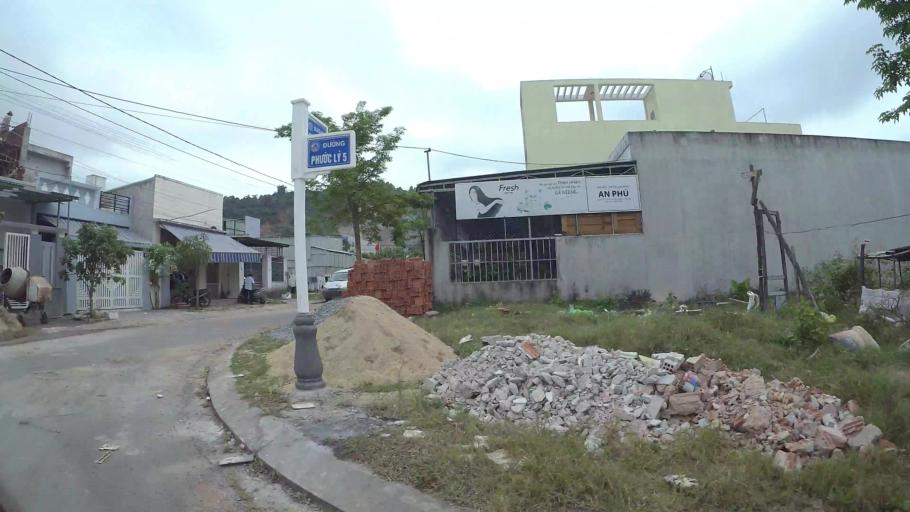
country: VN
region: Da Nang
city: Lien Chieu
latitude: 16.0429
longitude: 108.1690
